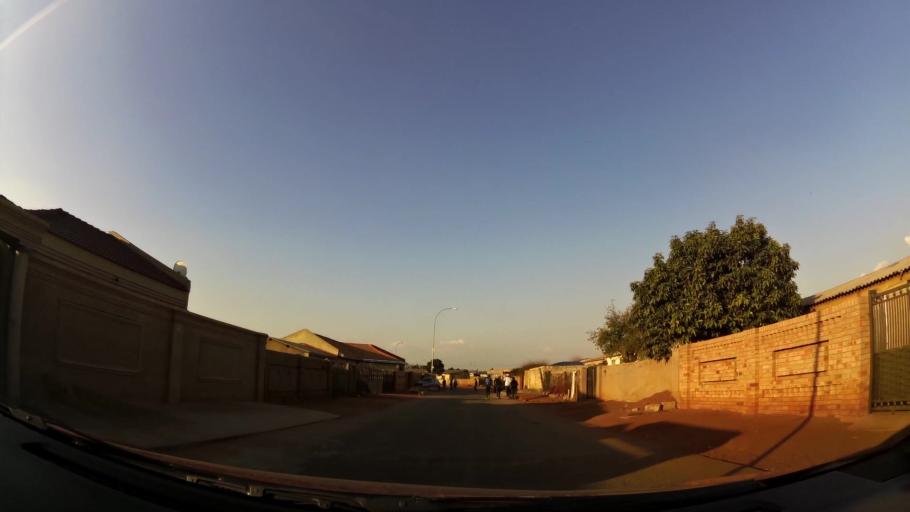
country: ZA
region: Gauteng
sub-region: City of Johannesburg Metropolitan Municipality
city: Soweto
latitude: -26.2250
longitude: 27.8562
